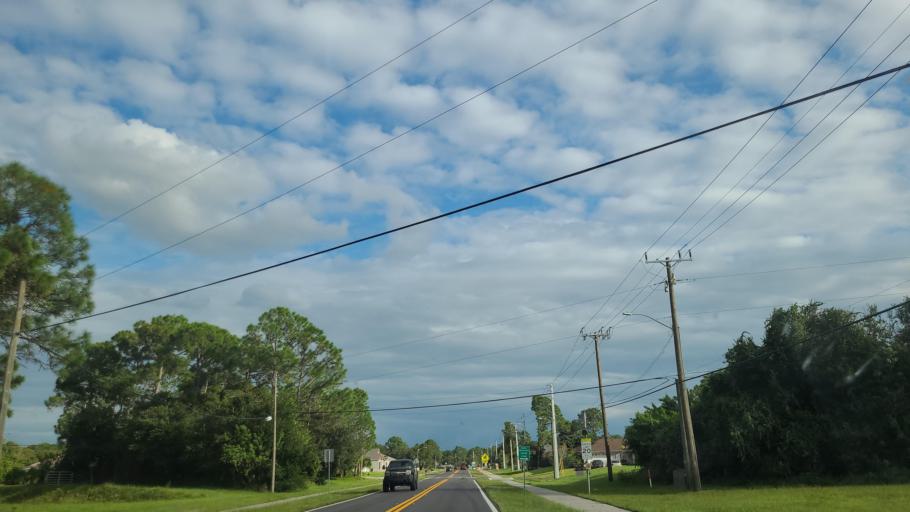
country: US
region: Florida
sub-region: Brevard County
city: June Park
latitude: 27.9919
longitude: -80.6947
